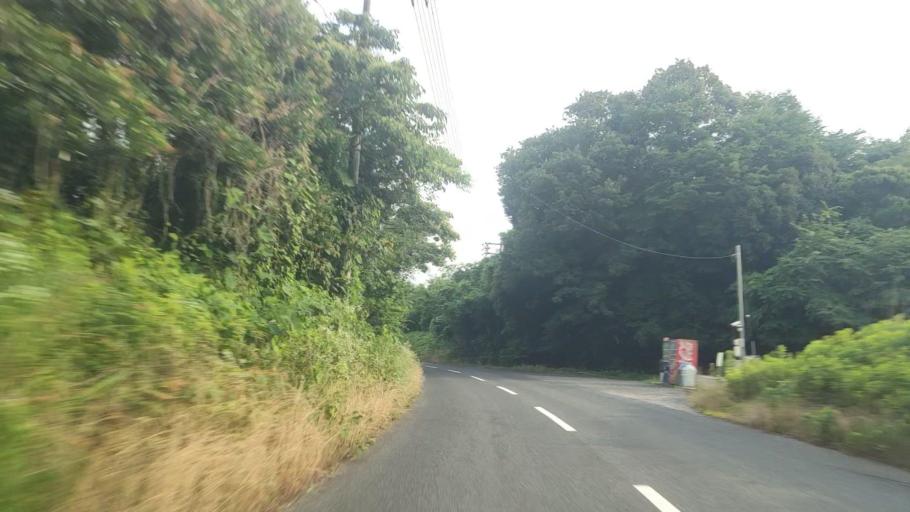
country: JP
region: Tottori
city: Kurayoshi
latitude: 35.3982
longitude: 133.7732
